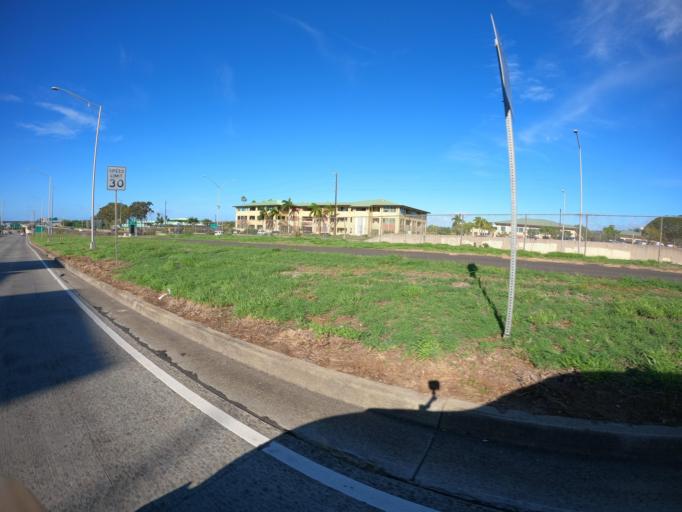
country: US
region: Hawaii
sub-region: Honolulu County
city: Honolulu
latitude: 21.3371
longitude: -157.8847
